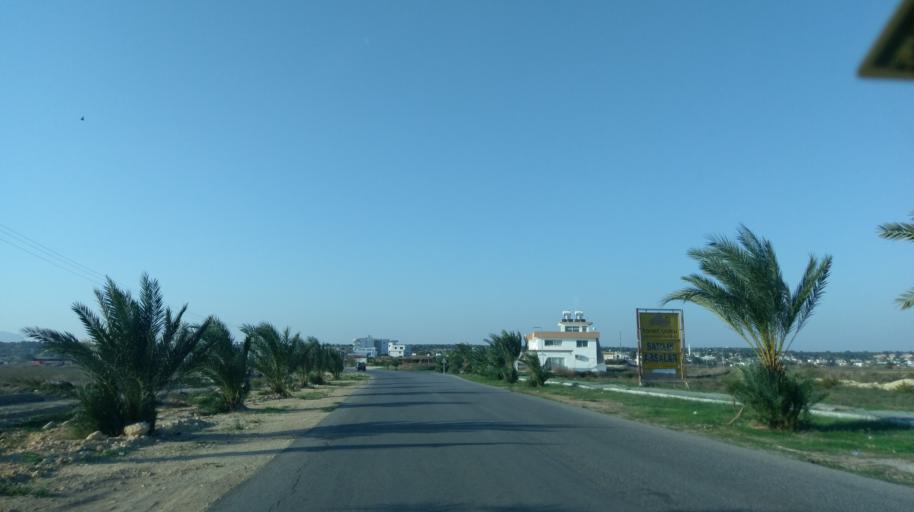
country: CY
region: Ammochostos
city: Leonarisso
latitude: 35.3702
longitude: 34.0733
